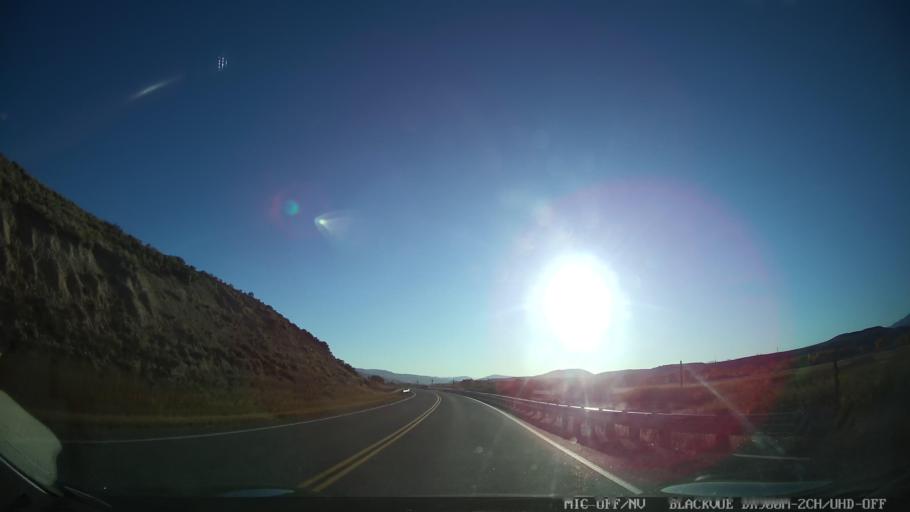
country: US
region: Colorado
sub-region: Grand County
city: Kremmling
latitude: 40.0566
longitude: -106.3168
